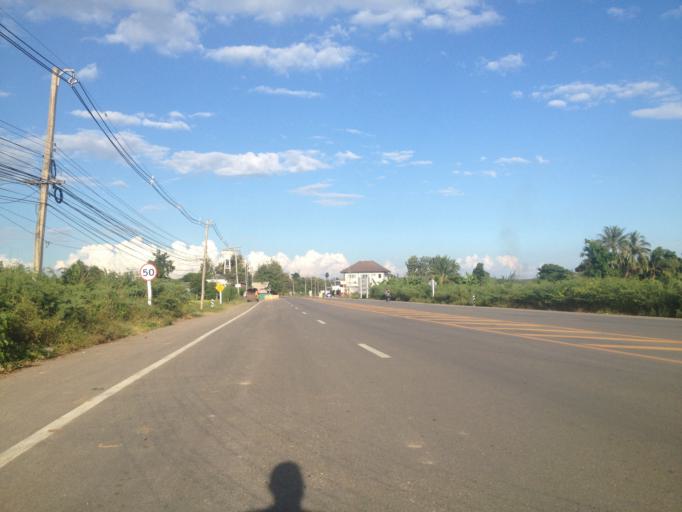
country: TH
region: Chiang Mai
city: San Pa Tong
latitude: 18.6068
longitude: 98.8369
